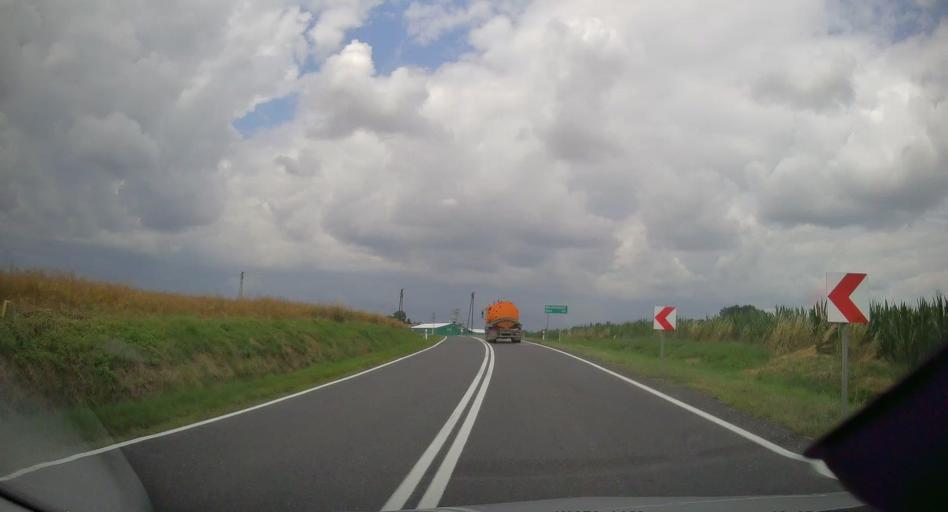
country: PL
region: Opole Voivodeship
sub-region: Powiat prudnicki
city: Prudnik
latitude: 50.3600
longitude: 17.5526
